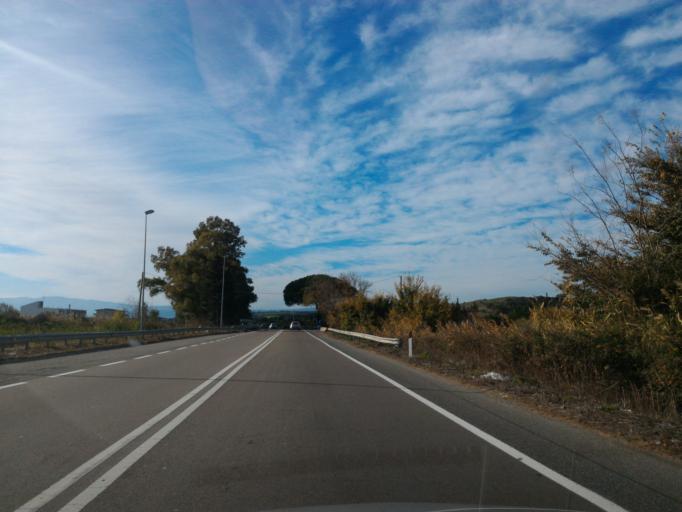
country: IT
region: Calabria
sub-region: Provincia di Catanzaro
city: Barone
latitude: 38.8683
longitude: 16.6882
